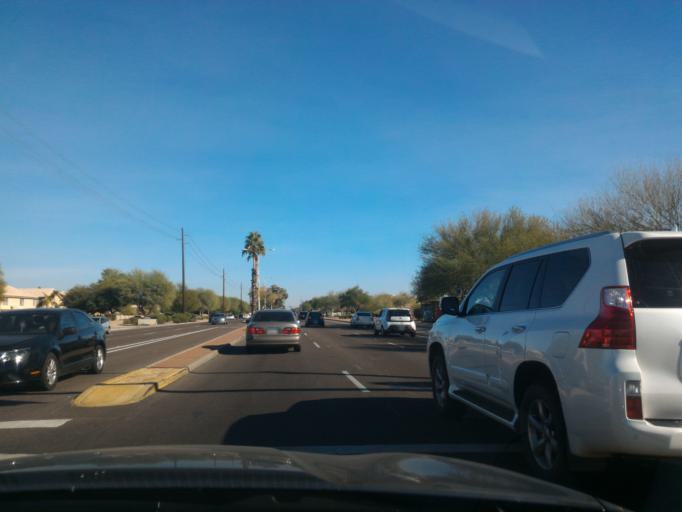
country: US
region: Arizona
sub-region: Maricopa County
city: Chandler
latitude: 33.3058
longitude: -111.8852
